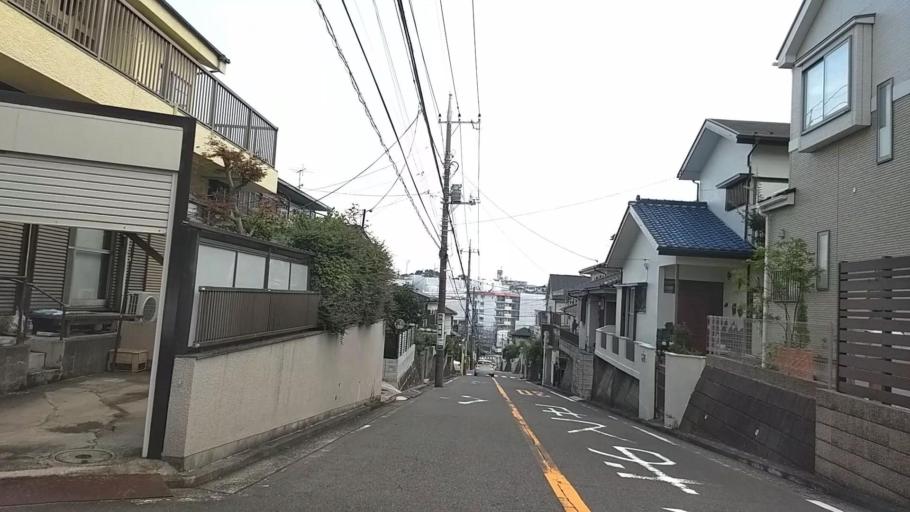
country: JP
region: Kanagawa
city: Yokohama
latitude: 35.4131
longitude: 139.5749
